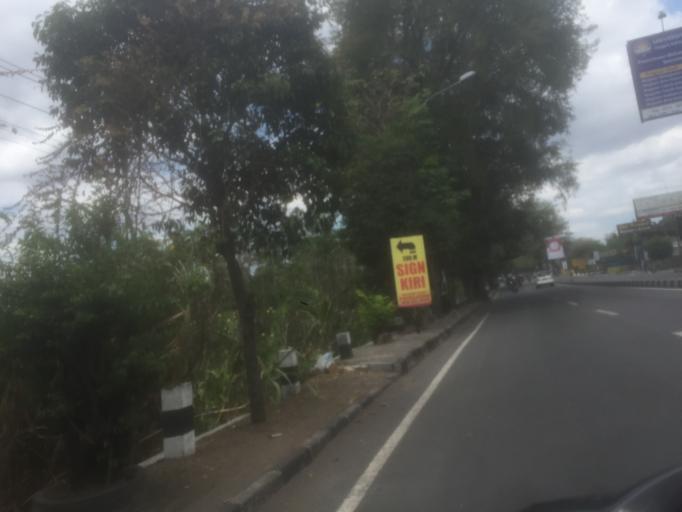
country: ID
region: Daerah Istimewa Yogyakarta
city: Melati
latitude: -7.7265
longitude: 110.3628
